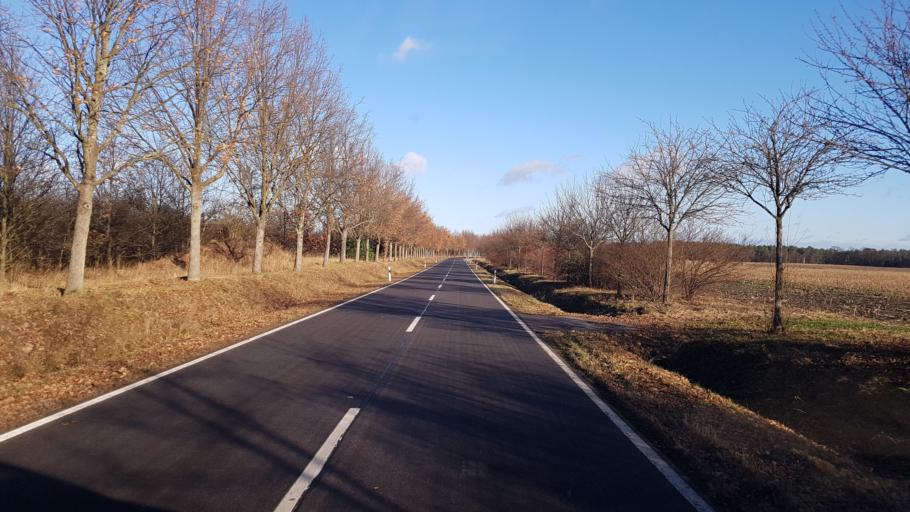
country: DE
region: Brandenburg
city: Forst
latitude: 51.7627
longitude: 14.5672
